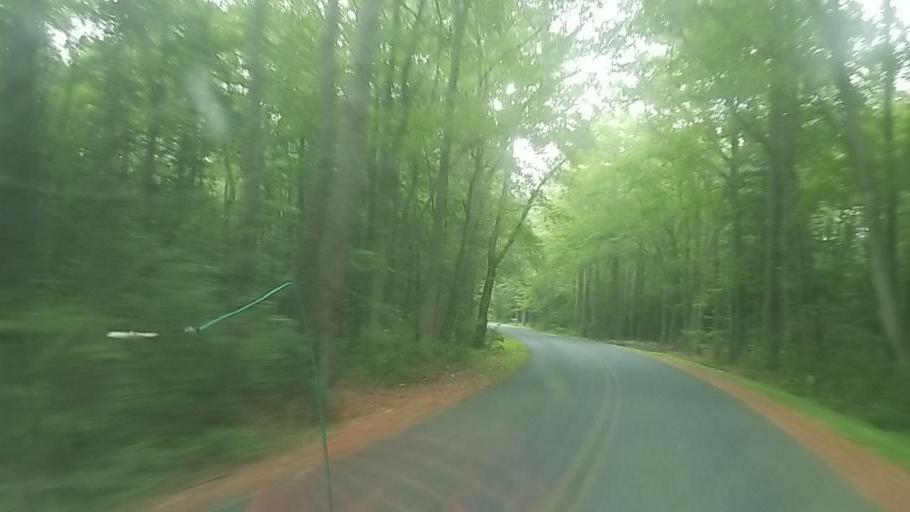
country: US
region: Maryland
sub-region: Wicomico County
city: Pittsville
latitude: 38.4143
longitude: -75.4771
